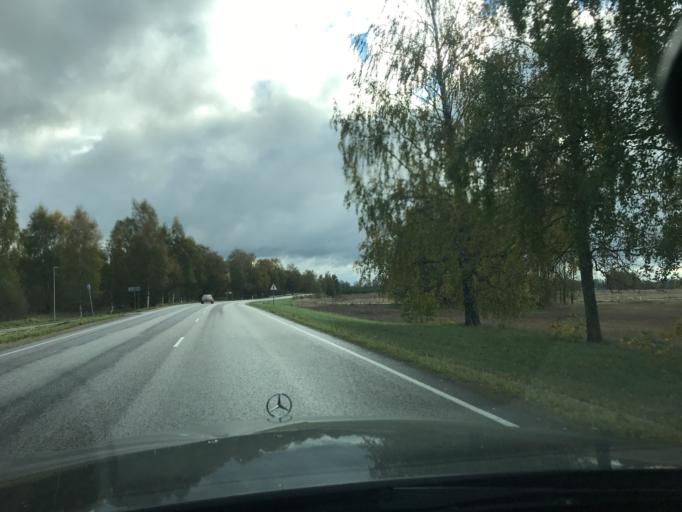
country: EE
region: Valgamaa
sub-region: Torva linn
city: Torva
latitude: 58.0295
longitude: 25.8544
